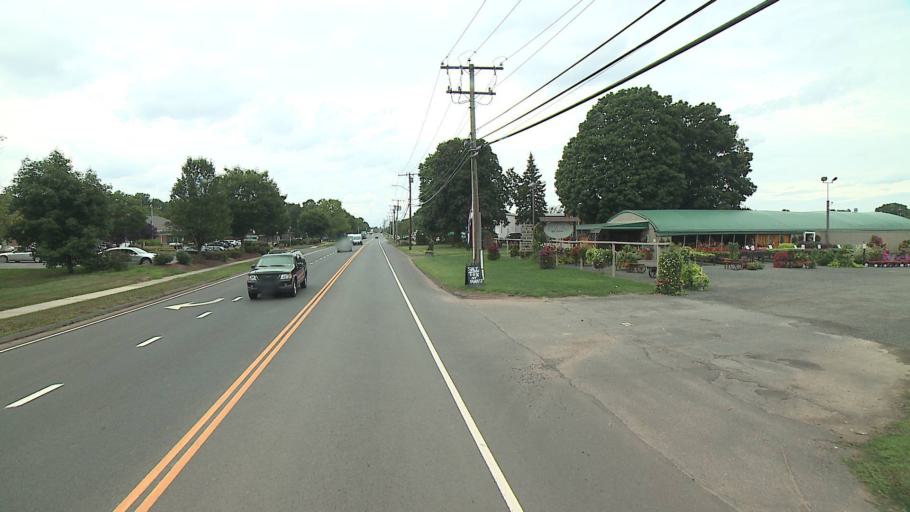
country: US
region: Connecticut
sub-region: Middlesex County
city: Cromwell
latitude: 41.6389
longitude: -72.6763
